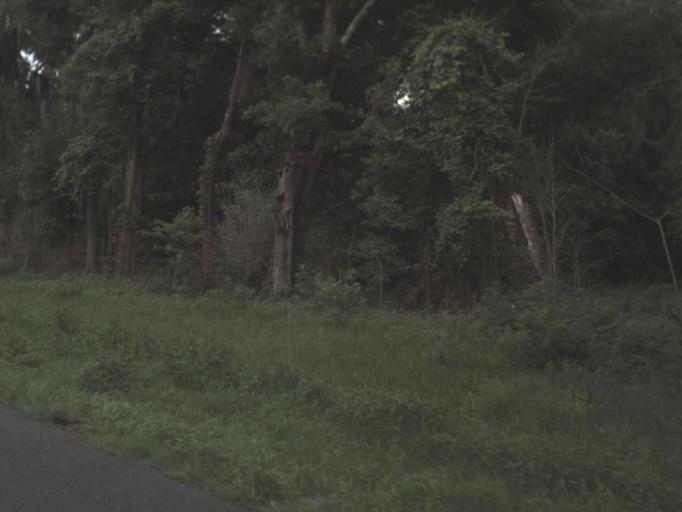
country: US
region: Florida
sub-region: Levy County
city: Williston
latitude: 29.3195
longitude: -82.4526
